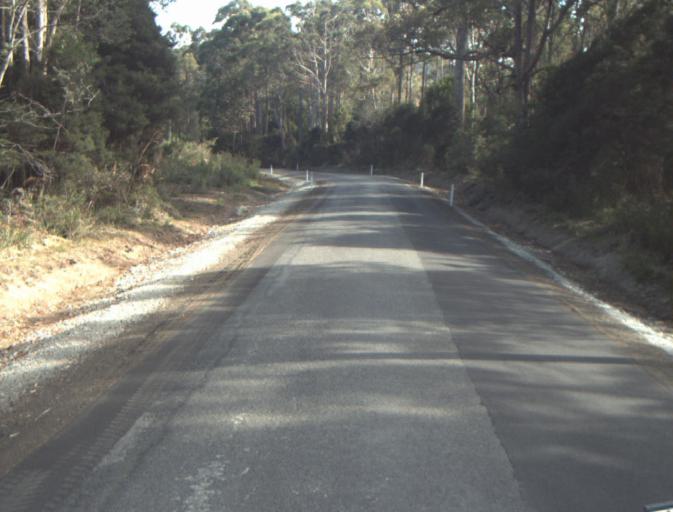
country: AU
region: Tasmania
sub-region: Launceston
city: Mayfield
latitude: -41.3079
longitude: 147.1989
